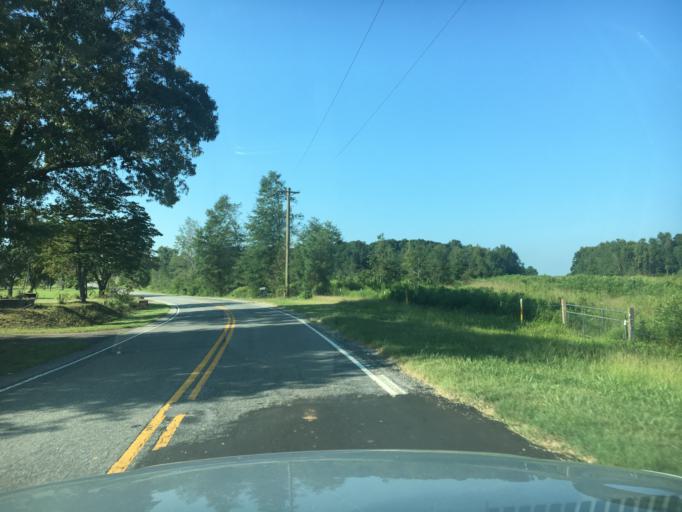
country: US
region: South Carolina
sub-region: Anderson County
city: Williamston
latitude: 34.6272
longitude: -82.3490
